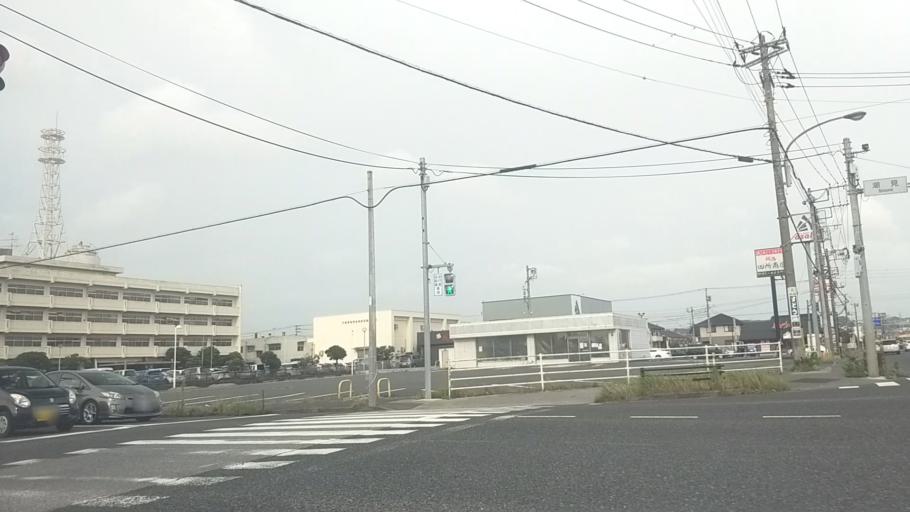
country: JP
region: Chiba
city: Kisarazu
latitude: 35.3699
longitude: 139.9169
